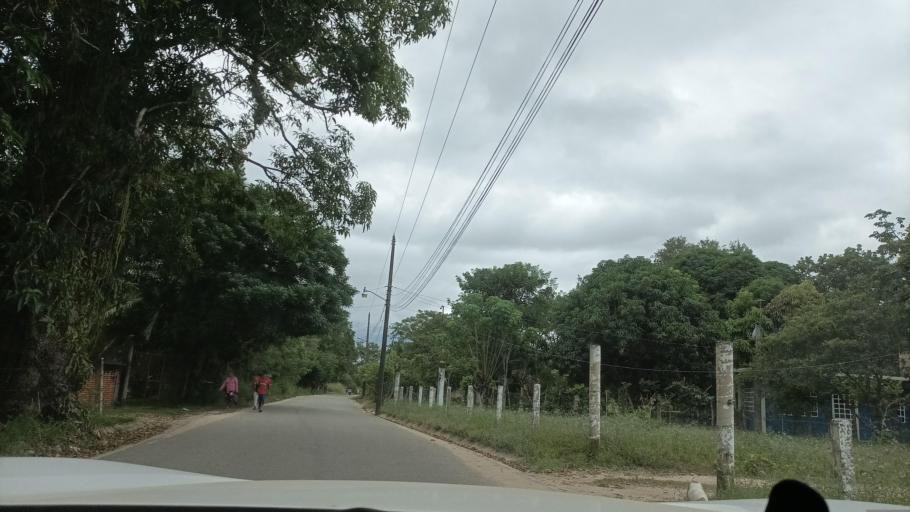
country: MX
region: Veracruz
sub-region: Cosoleacaque
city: Coacotla
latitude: 17.9510
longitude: -94.7119
